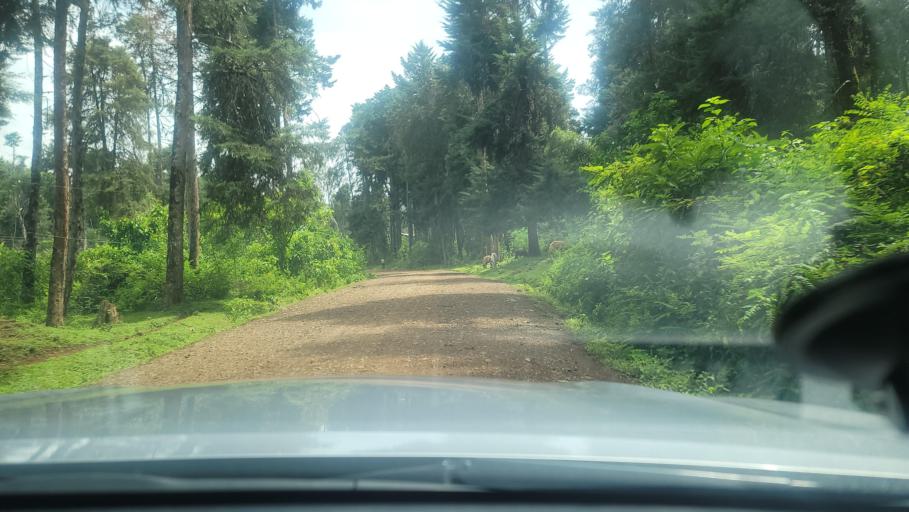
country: ET
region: Oromiya
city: Agaro
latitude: 7.7924
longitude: 36.4184
